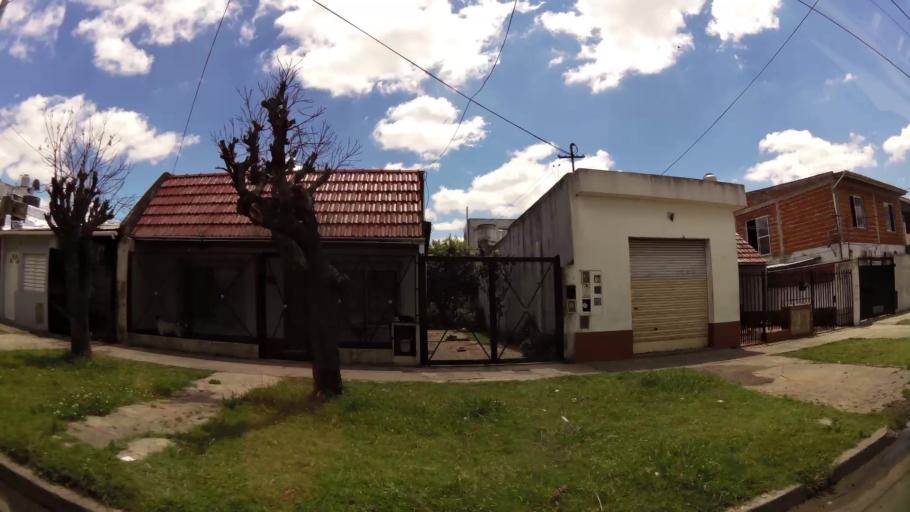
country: AR
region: Buenos Aires
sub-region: Partido de Lanus
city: Lanus
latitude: -34.7214
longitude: -58.4133
